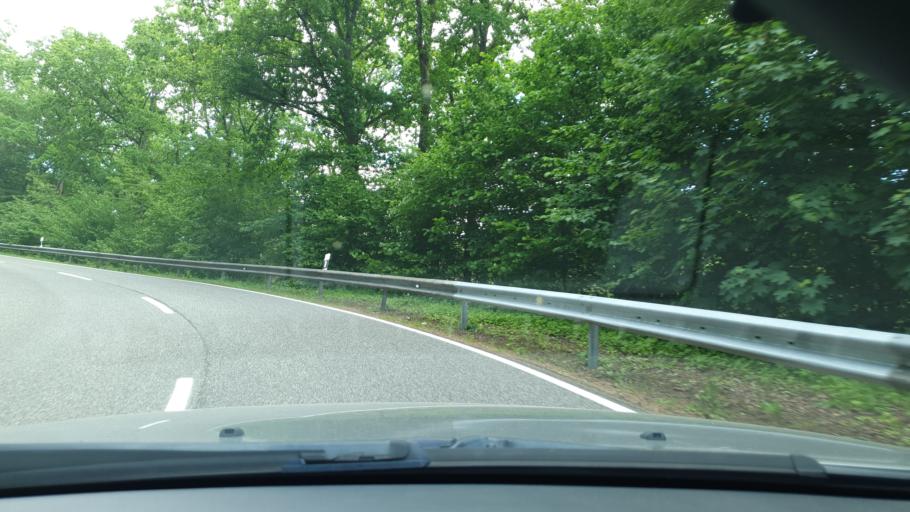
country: DE
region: Rheinland-Pfalz
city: Battweiler
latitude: 49.2777
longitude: 7.4547
